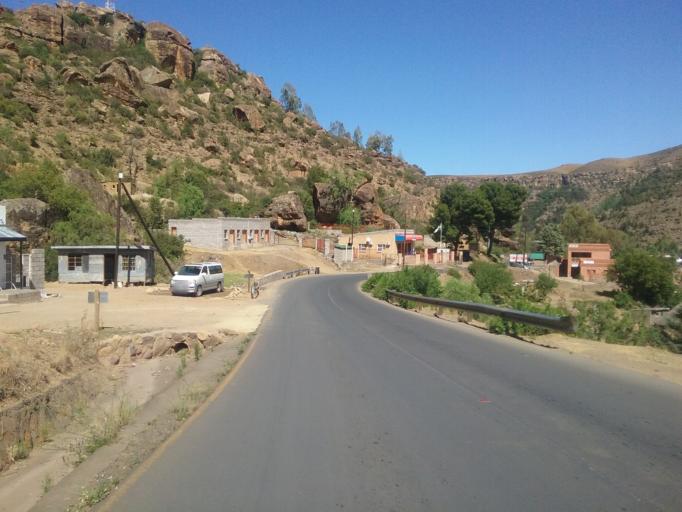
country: LS
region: Quthing
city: Quthing
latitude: -30.4008
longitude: 27.6960
